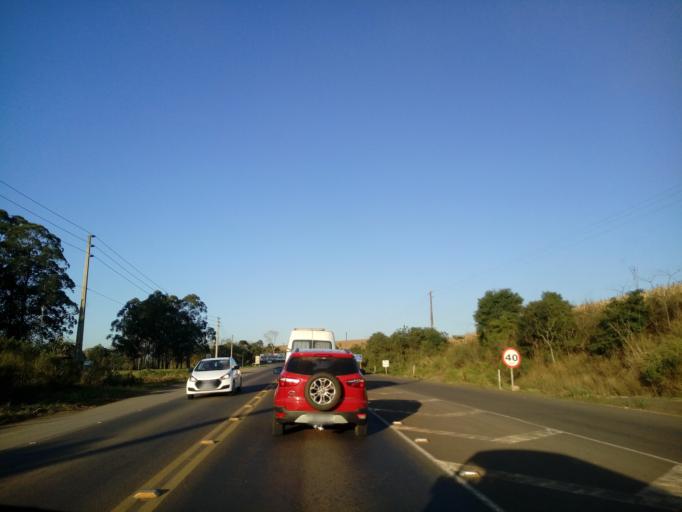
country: BR
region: Santa Catarina
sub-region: Chapeco
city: Chapeco
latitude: -27.2280
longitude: -52.6781
